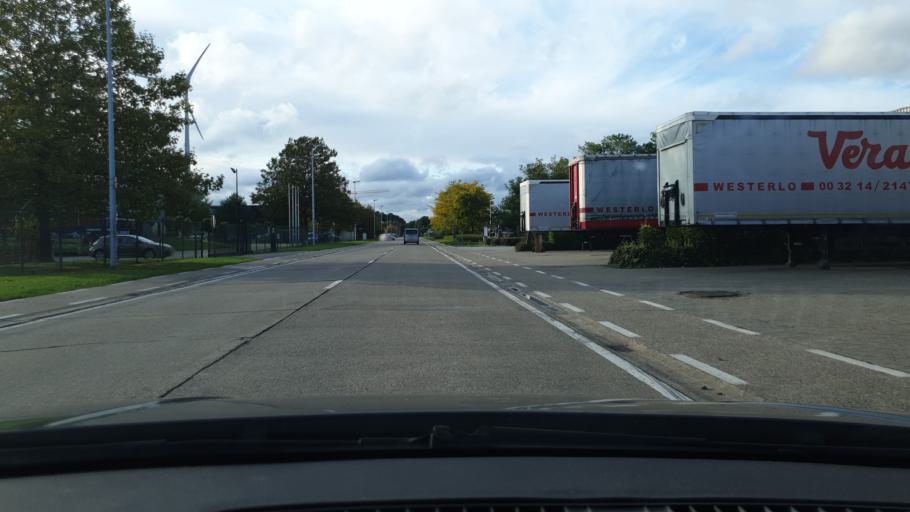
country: BE
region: Flanders
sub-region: Provincie Antwerpen
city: Olen
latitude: 51.1485
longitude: 4.9158
